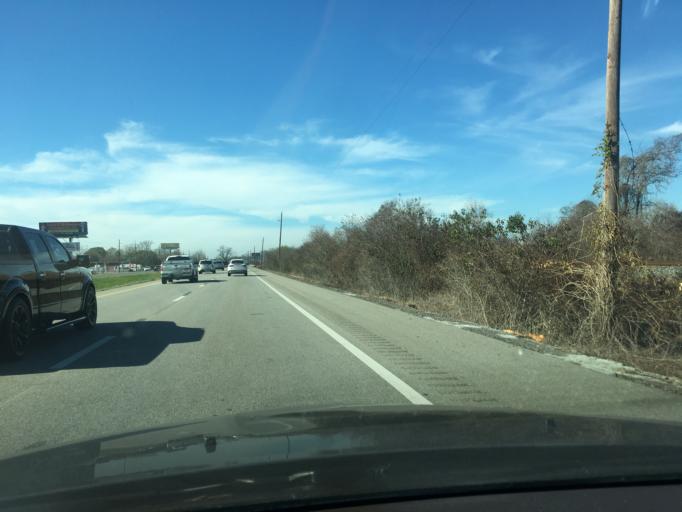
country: US
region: Texas
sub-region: Fort Bend County
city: Pecan Grove
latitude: 29.5974
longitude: -95.7273
